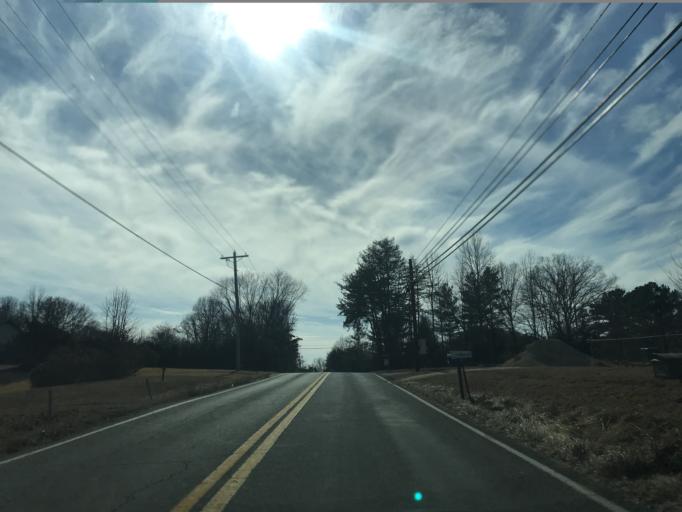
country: US
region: Maryland
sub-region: Charles County
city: Potomac Heights
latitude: 38.5648
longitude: -77.1283
